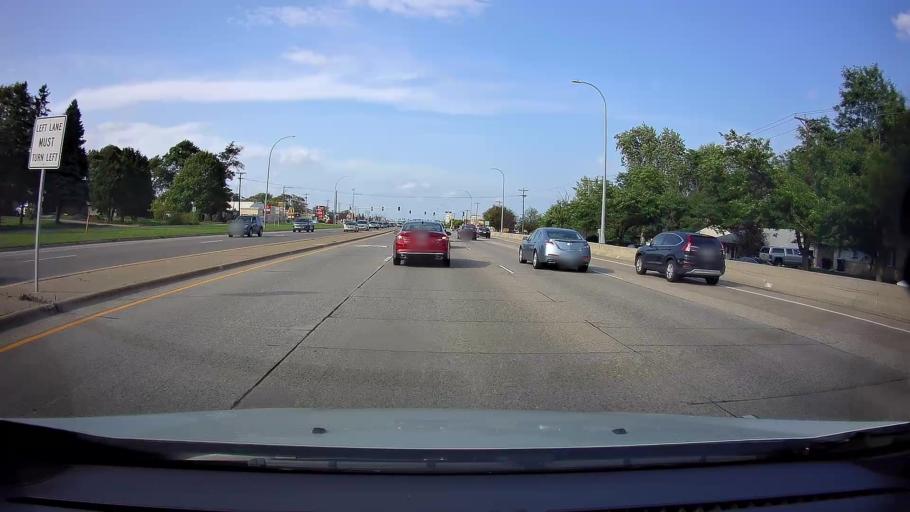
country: US
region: Minnesota
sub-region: Ramsey County
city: Falcon Heights
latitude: 45.0016
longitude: -93.1664
